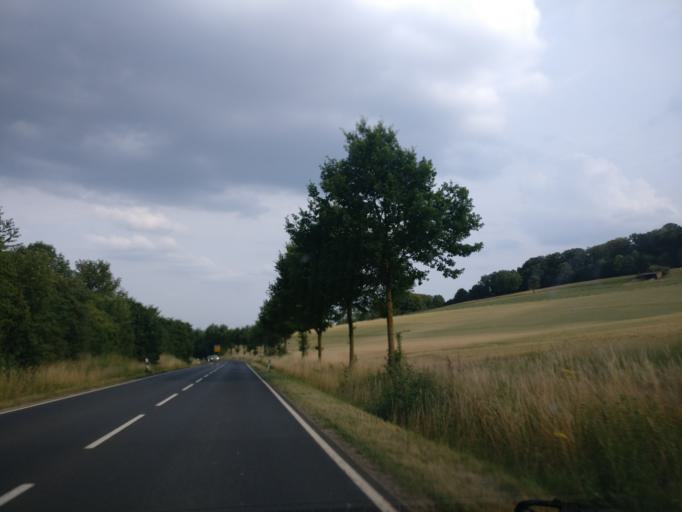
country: DE
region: Lower Saxony
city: Bovenden
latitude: 51.5808
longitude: 9.8691
